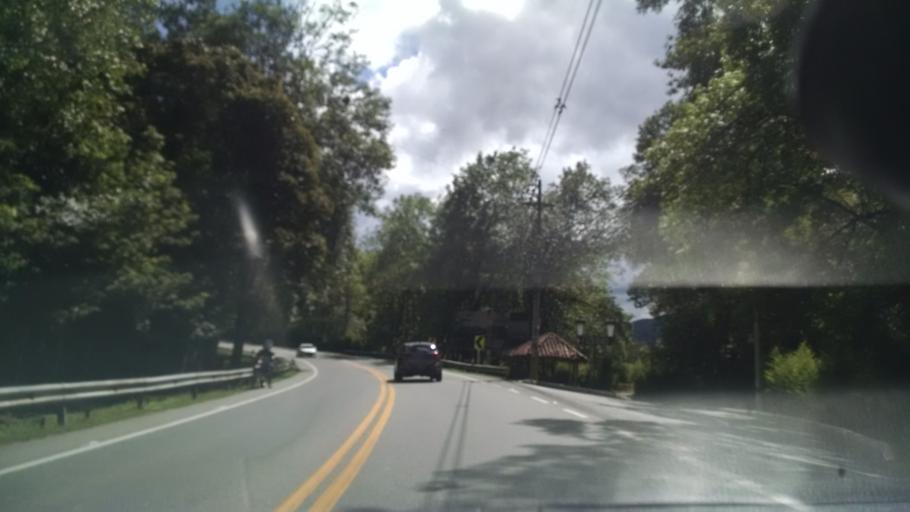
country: CO
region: Antioquia
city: El Retiro
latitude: 6.1003
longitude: -75.5055
